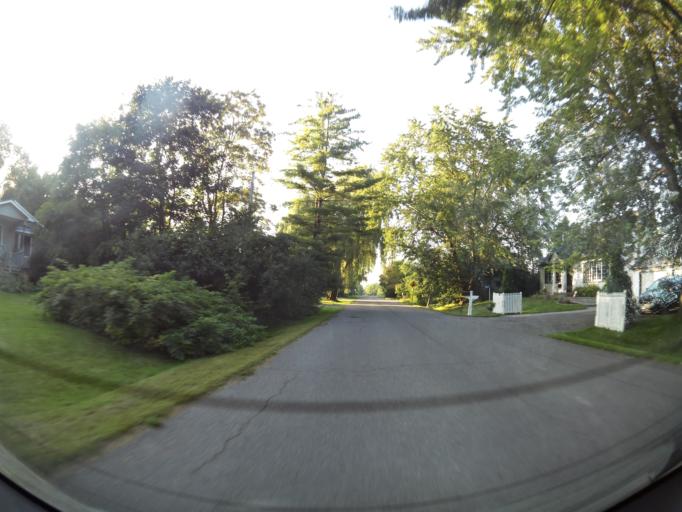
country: CA
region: Ontario
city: Clarence-Rockland
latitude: 45.5078
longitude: -75.4247
